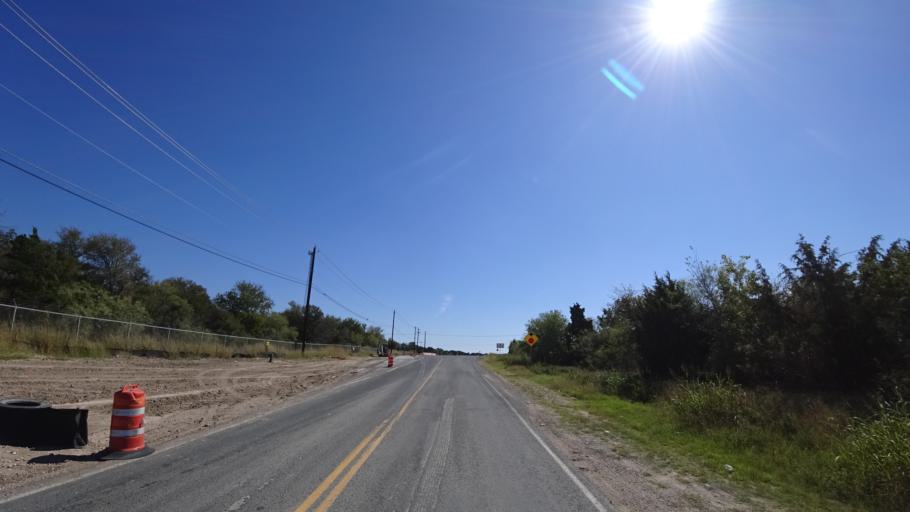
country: US
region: Texas
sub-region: Travis County
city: Hornsby Bend
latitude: 30.2764
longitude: -97.6018
